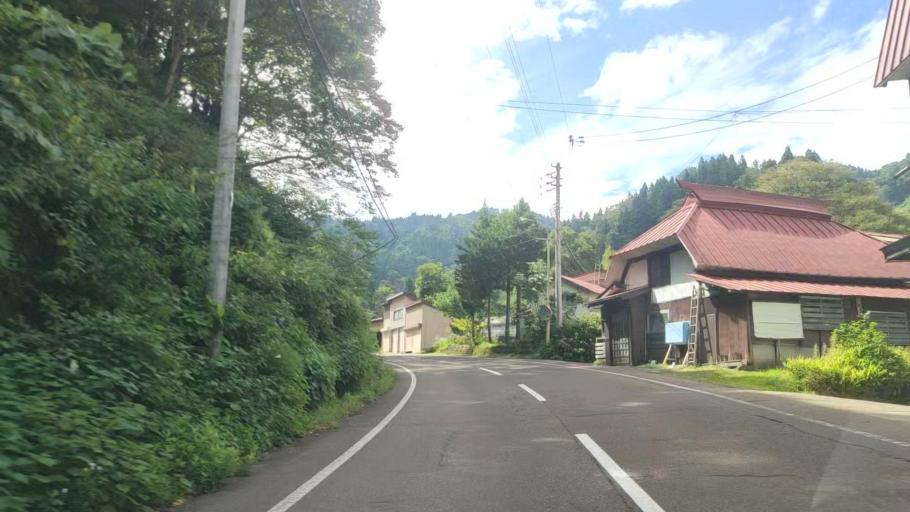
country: JP
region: Niigata
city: Arai
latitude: 36.9301
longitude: 138.2984
